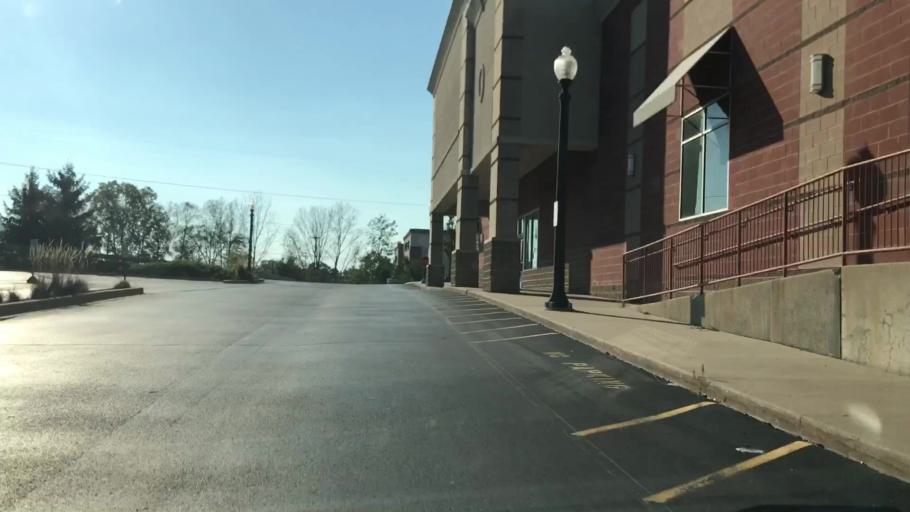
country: US
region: Wisconsin
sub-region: Waukesha County
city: Menomonee Falls
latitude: 43.1929
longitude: -88.1451
